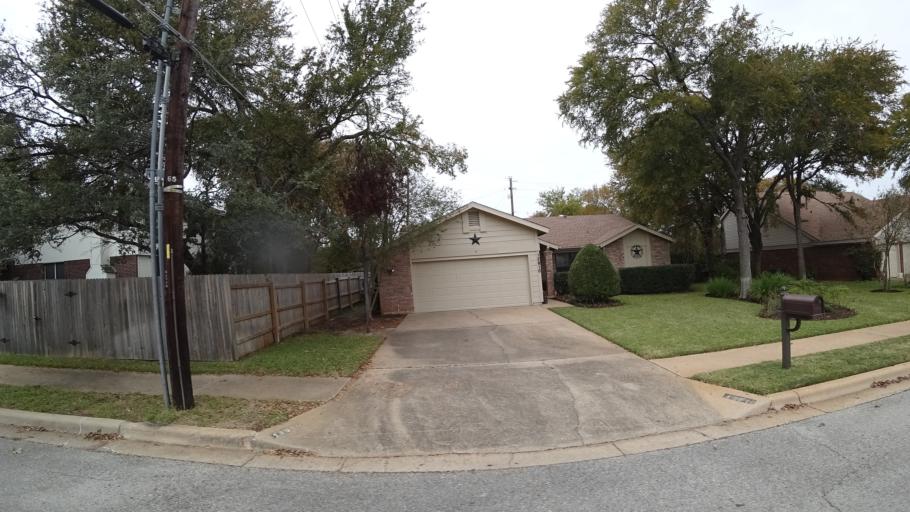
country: US
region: Texas
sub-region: Travis County
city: Wells Branch
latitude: 30.4315
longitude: -97.7190
